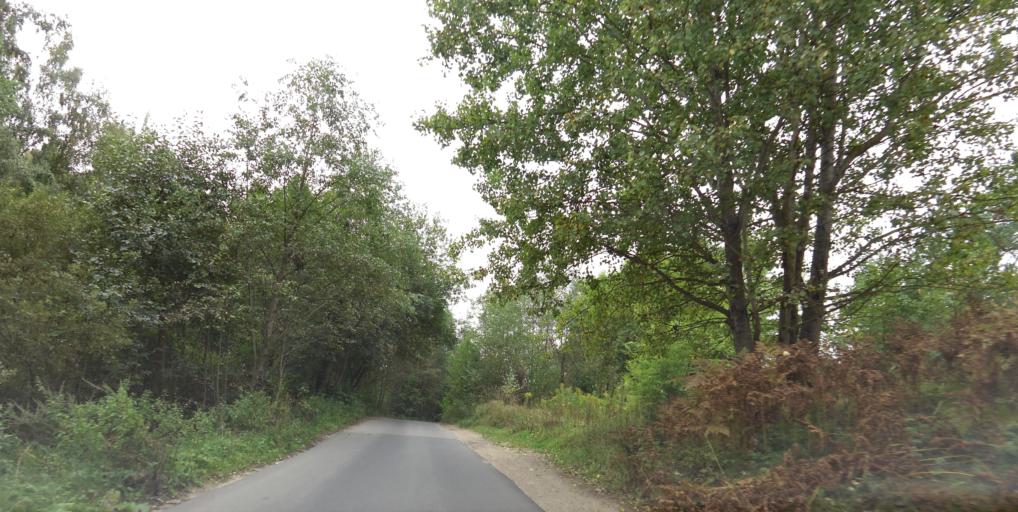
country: LT
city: Grigiskes
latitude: 54.7588
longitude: 25.0371
